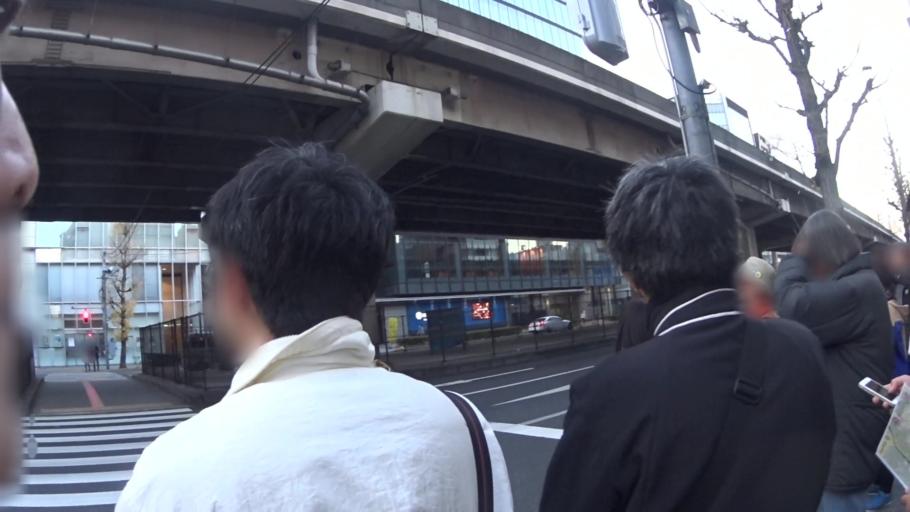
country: JP
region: Tokyo
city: Tokyo
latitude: 35.7007
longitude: 139.7757
